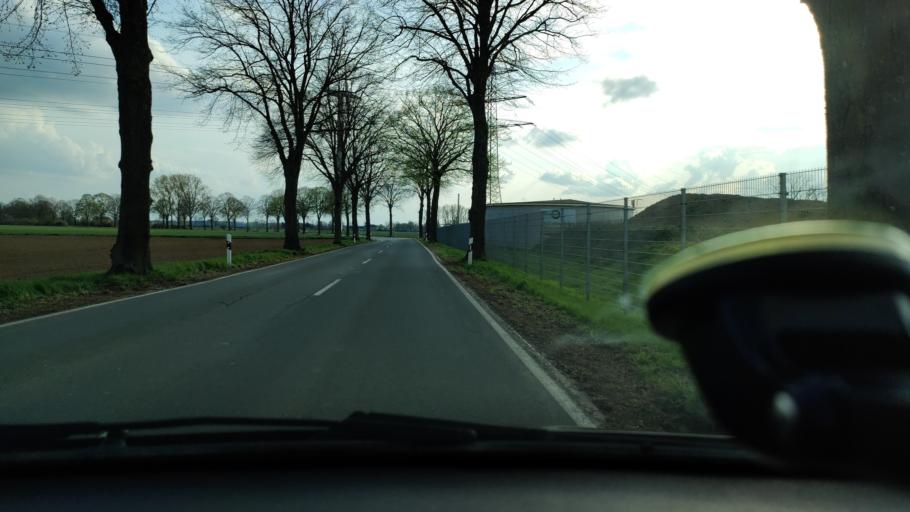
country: DE
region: North Rhine-Westphalia
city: Rees
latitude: 51.7390
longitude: 6.3789
